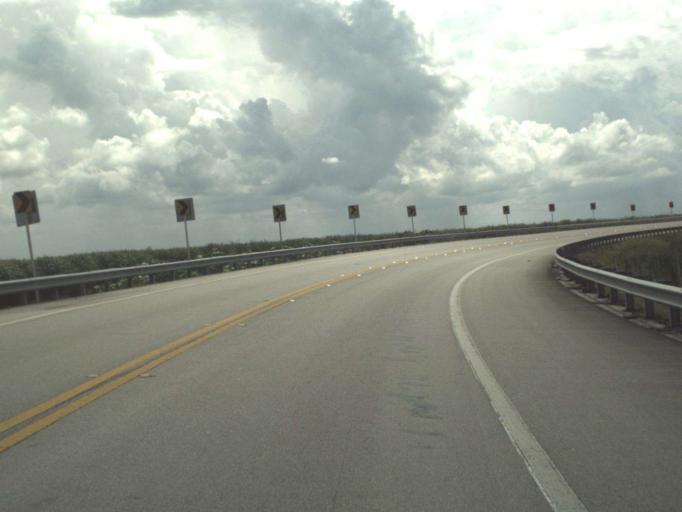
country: US
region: Florida
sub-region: Palm Beach County
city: Pahokee
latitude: 26.7715
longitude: -80.6533
